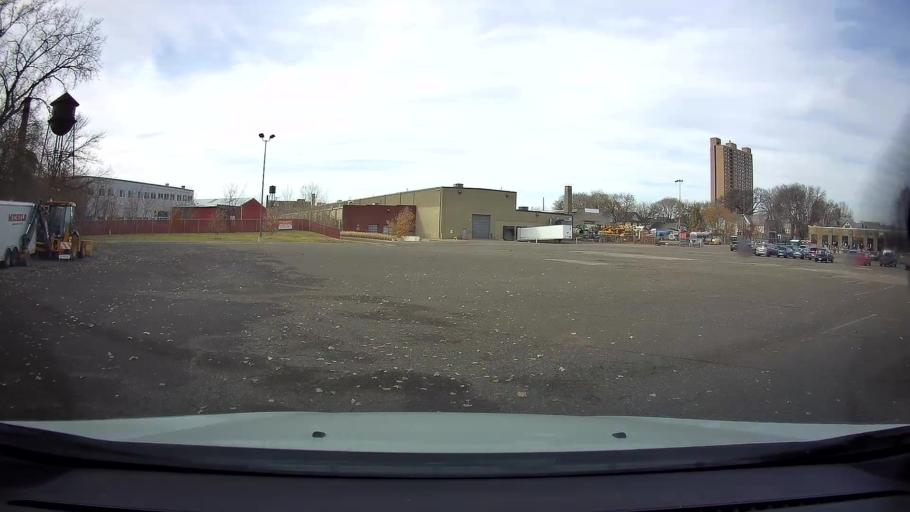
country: US
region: Minnesota
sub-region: Hennepin County
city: Minneapolis
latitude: 45.0035
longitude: -93.2440
